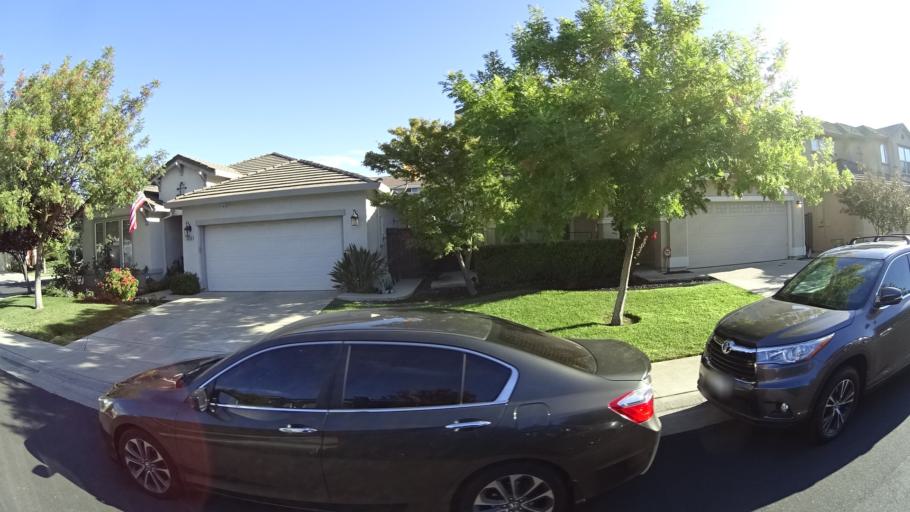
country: US
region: California
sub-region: Sacramento County
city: Laguna
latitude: 38.4029
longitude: -121.4707
